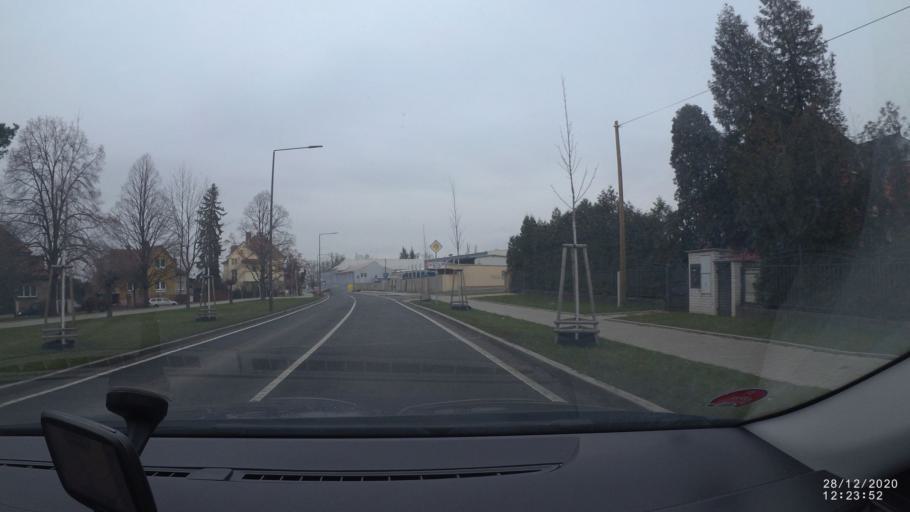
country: CZ
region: Central Bohemia
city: Brandys nad Labem-Stara Boleslav
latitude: 50.1789
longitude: 14.6550
